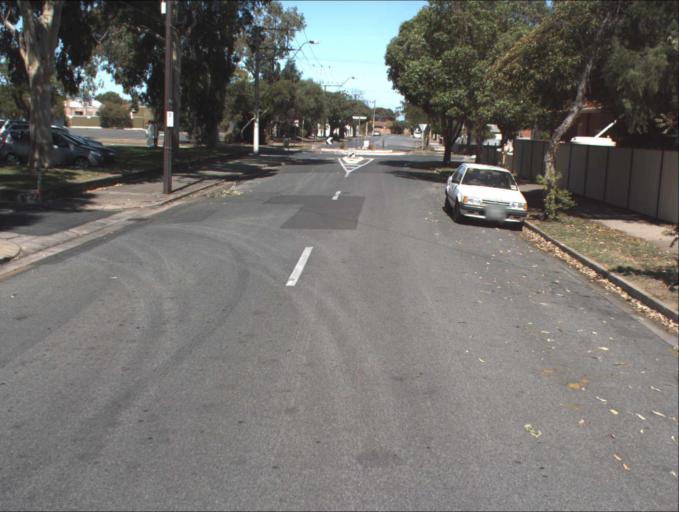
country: AU
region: South Australia
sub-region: Port Adelaide Enfield
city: Cheltenham
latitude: -34.8637
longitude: 138.5184
